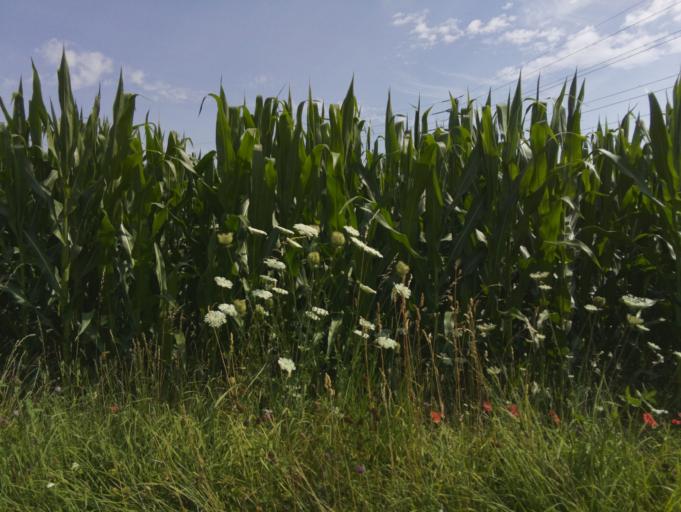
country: CH
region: Zurich
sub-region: Bezirk Andelfingen
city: Henggart
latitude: 47.5767
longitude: 8.6779
